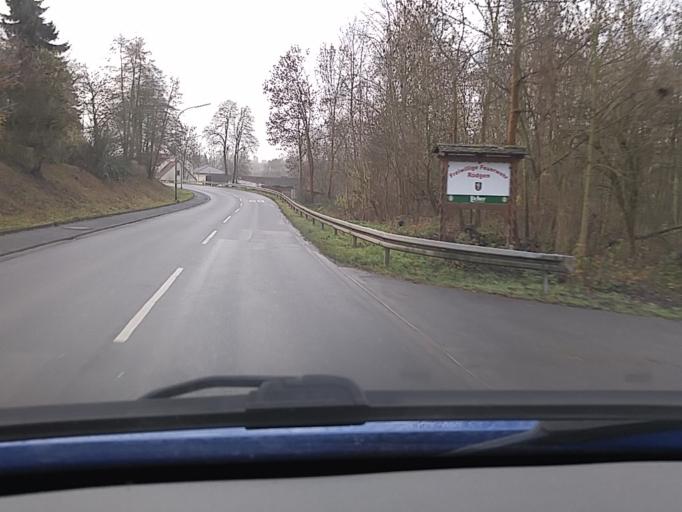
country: DE
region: Hesse
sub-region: Regierungsbezirk Darmstadt
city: Bad Nauheim
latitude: 50.3695
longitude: 8.7645
